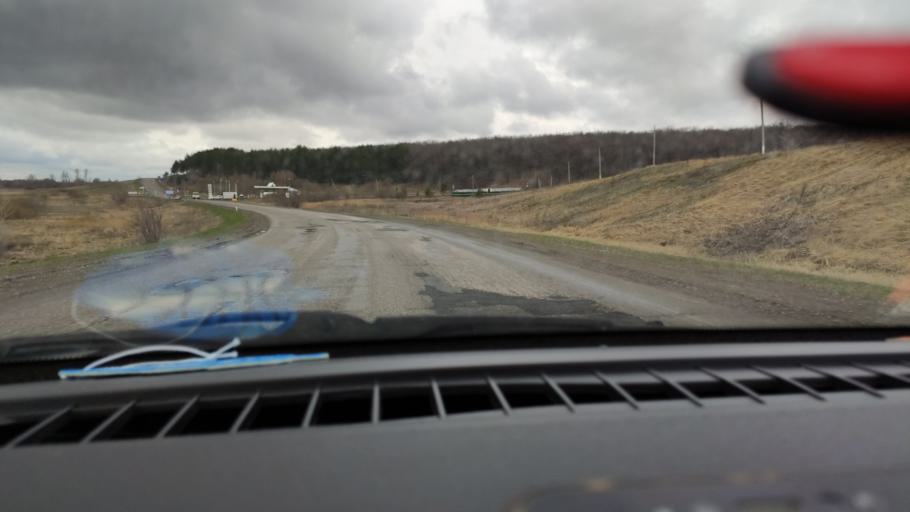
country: RU
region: Tatarstan
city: Nurlat
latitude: 54.3867
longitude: 50.7482
